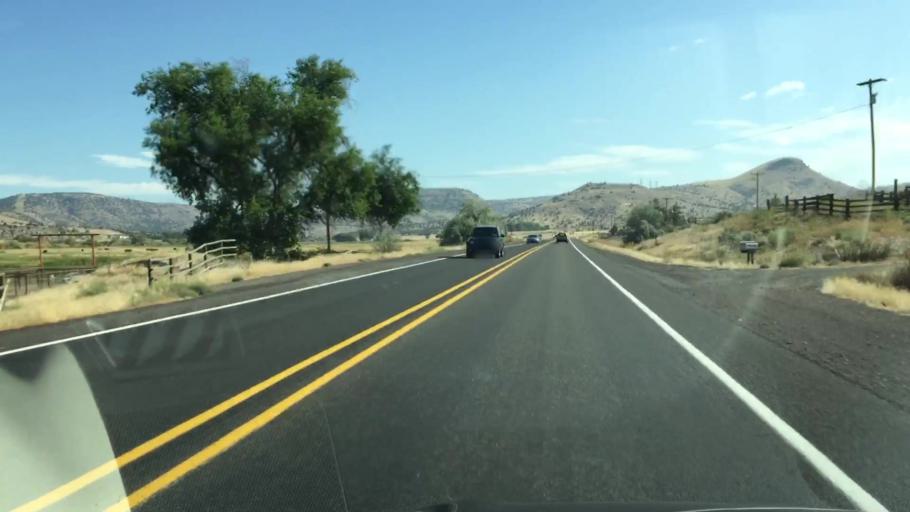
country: US
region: Oregon
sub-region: Jefferson County
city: Madras
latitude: 44.7977
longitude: -120.9479
